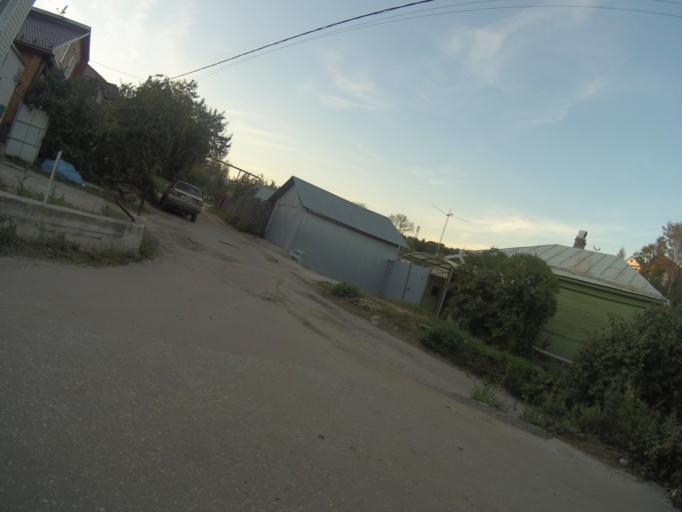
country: RU
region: Vladimir
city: Vladimir
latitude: 56.1197
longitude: 40.3946
